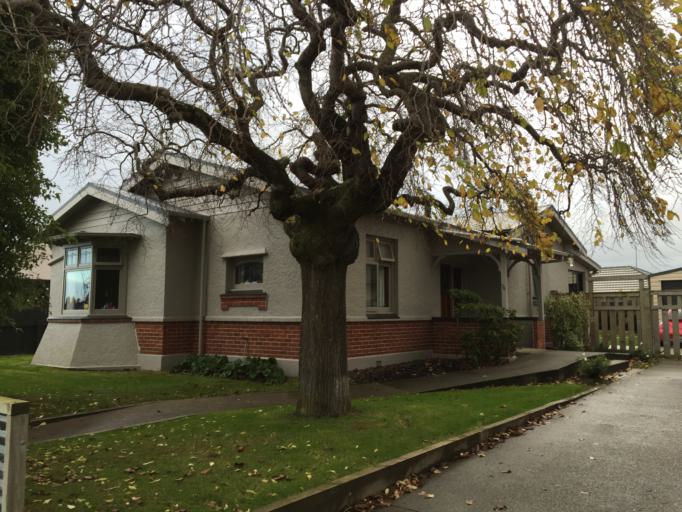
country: NZ
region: Southland
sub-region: Invercargill City
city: Invercargill
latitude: -46.4079
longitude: 168.3712
